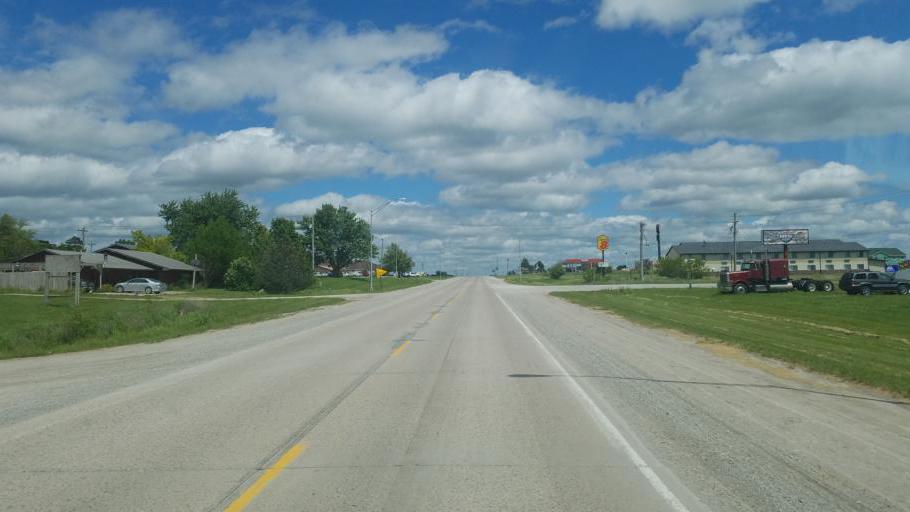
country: US
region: Iowa
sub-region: Decatur County
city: Lamoni
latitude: 40.6236
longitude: -93.9005
